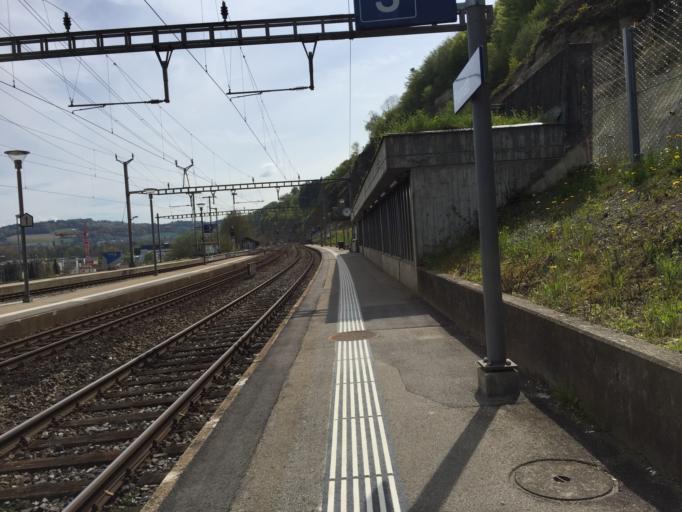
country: CH
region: Fribourg
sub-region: Sense District
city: Flamatt
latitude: 46.8882
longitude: 7.3201
